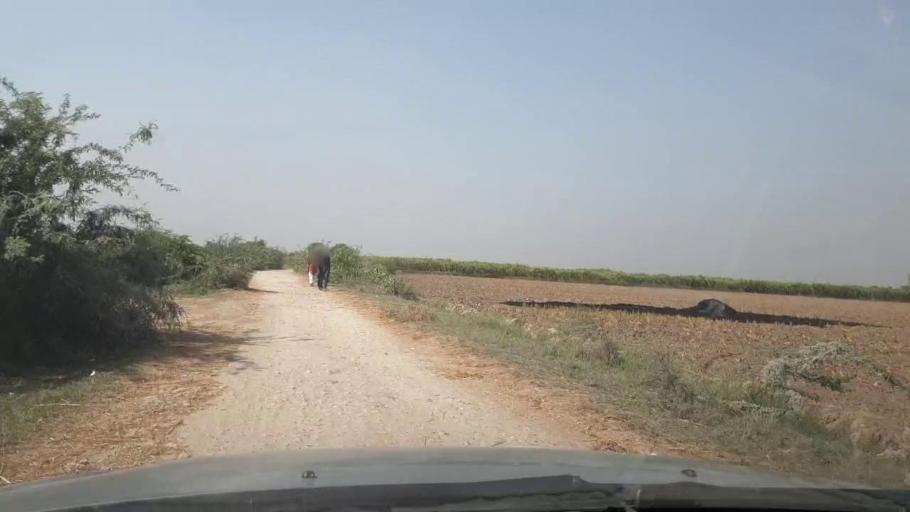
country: PK
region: Sindh
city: Bulri
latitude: 24.8687
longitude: 68.3235
